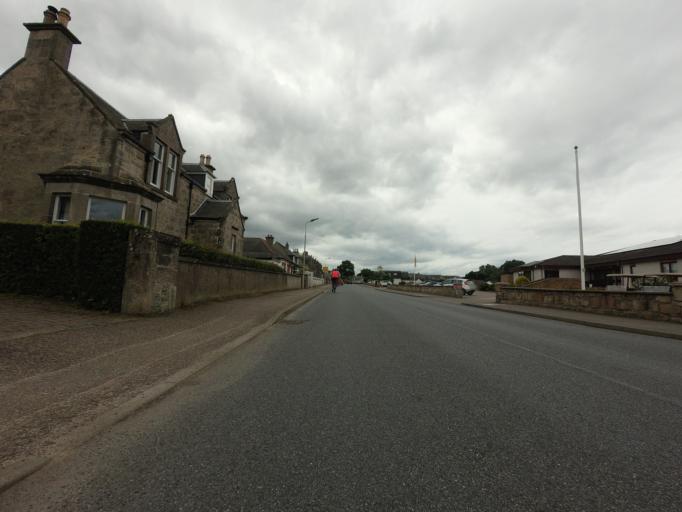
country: GB
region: Scotland
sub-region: Highland
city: Nairn
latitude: 57.5859
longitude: -3.8583
